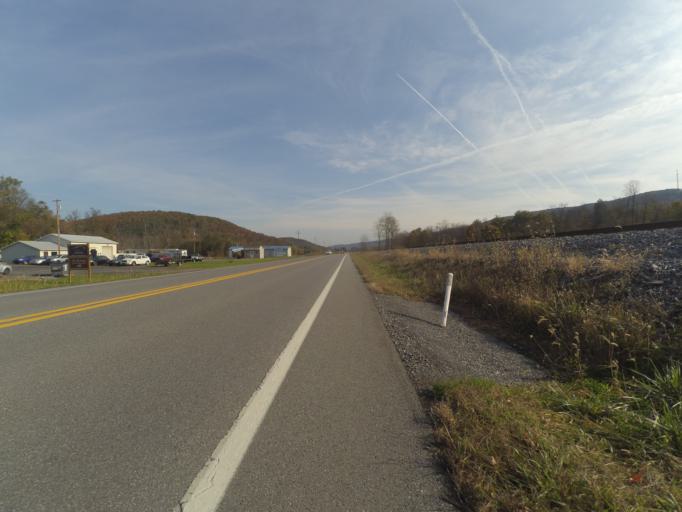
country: US
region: Pennsylvania
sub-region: Centre County
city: Stormstown
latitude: 40.8415
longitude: -77.9897
